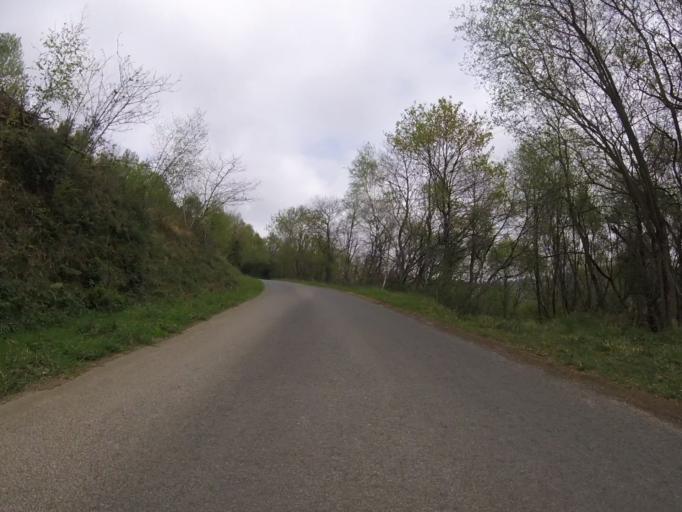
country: ES
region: Basque Country
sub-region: Provincia de Guipuzcoa
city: Zizurkil
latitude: 43.2176
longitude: -2.0901
